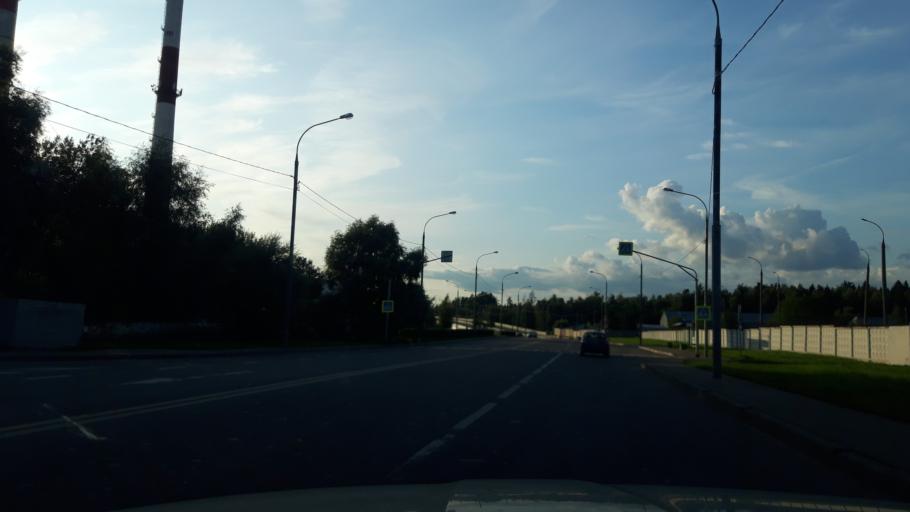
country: RU
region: Moscow
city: Zelenograd
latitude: 55.9912
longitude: 37.1664
